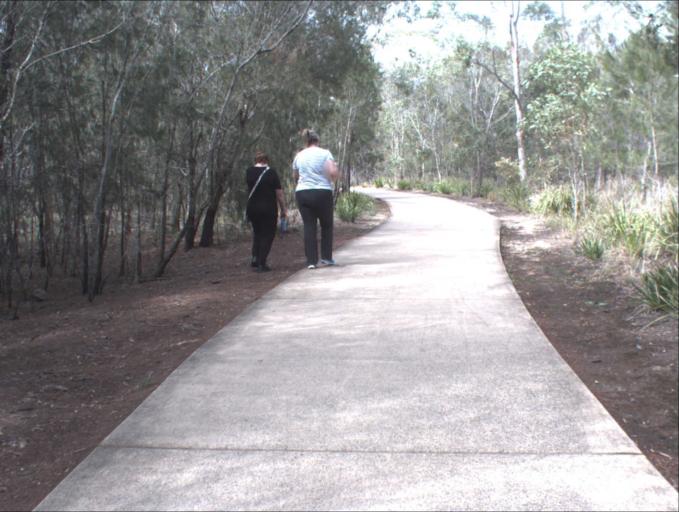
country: AU
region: Queensland
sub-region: Logan
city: Woodridge
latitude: -27.6641
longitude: 153.0738
